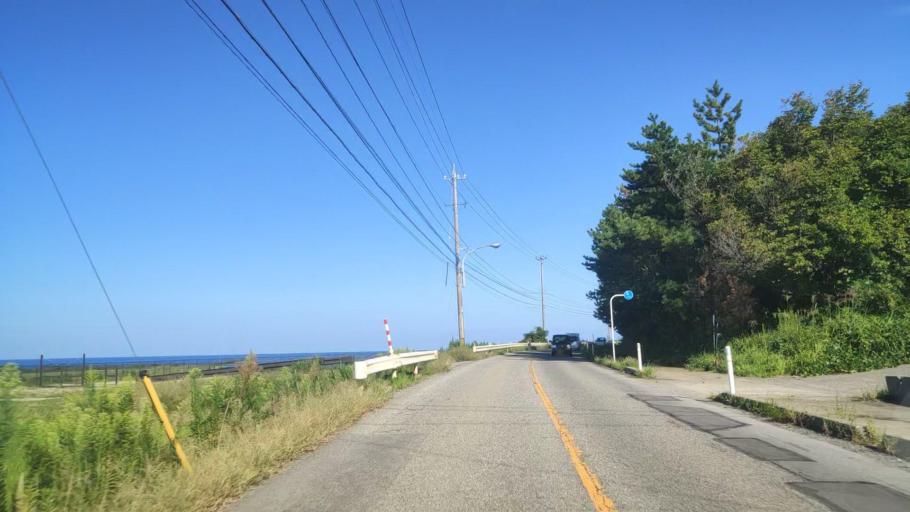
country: JP
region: Ishikawa
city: Hakui
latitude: 36.9291
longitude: 136.7572
